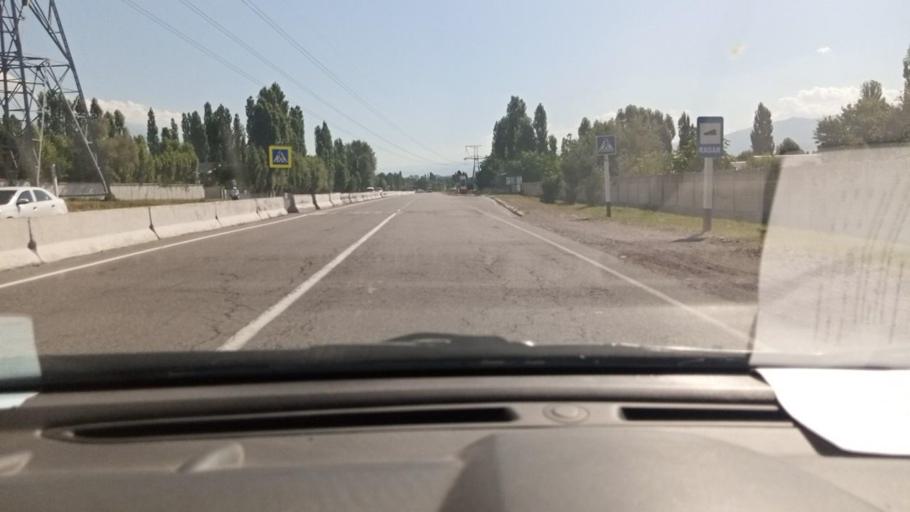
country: UZ
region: Toshkent
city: Angren
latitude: 40.9866
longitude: 70.0333
